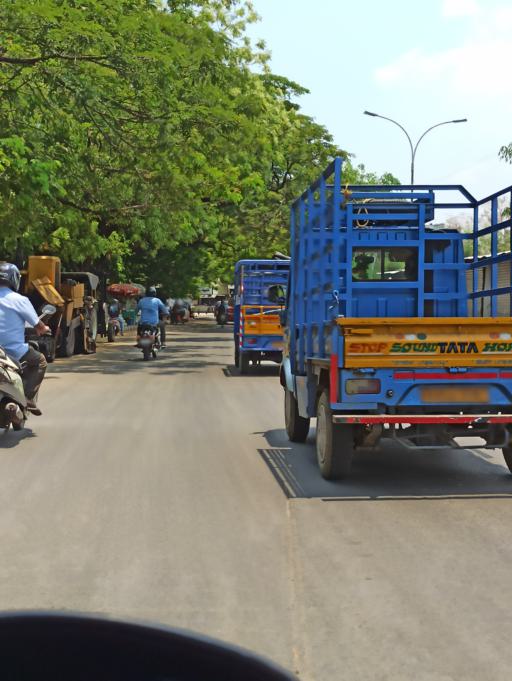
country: IN
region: Tamil Nadu
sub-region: Chennai
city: Chetput
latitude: 13.0874
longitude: 80.2346
